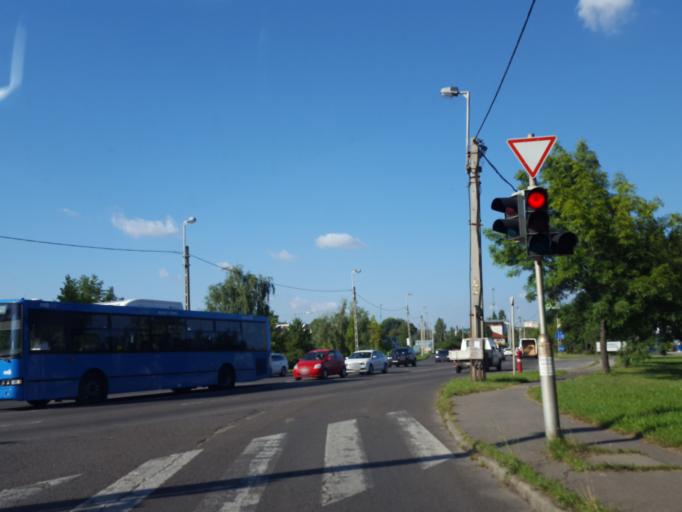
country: HU
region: Budapest
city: Budapest XI. keruelet
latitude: 47.4526
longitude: 19.0170
